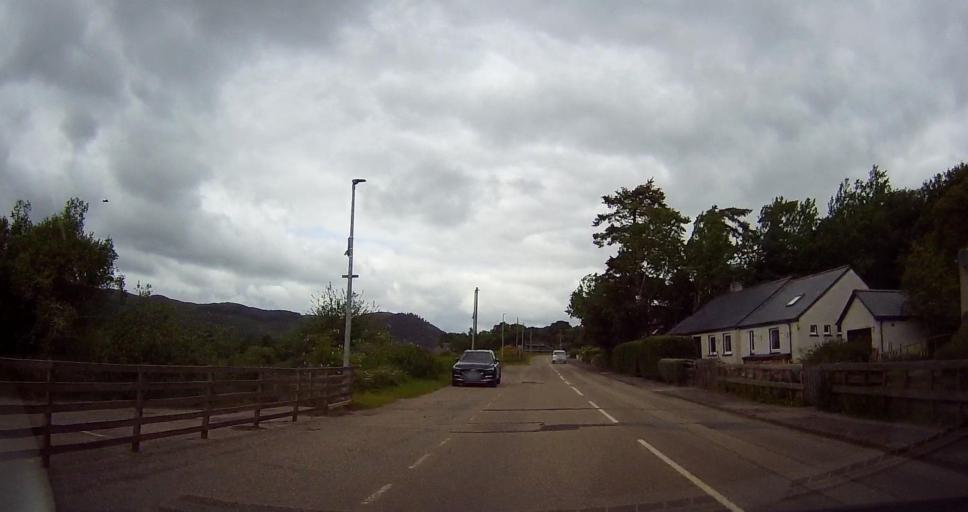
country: GB
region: Scotland
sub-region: Highland
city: Dornoch
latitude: 57.9867
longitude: -4.1531
